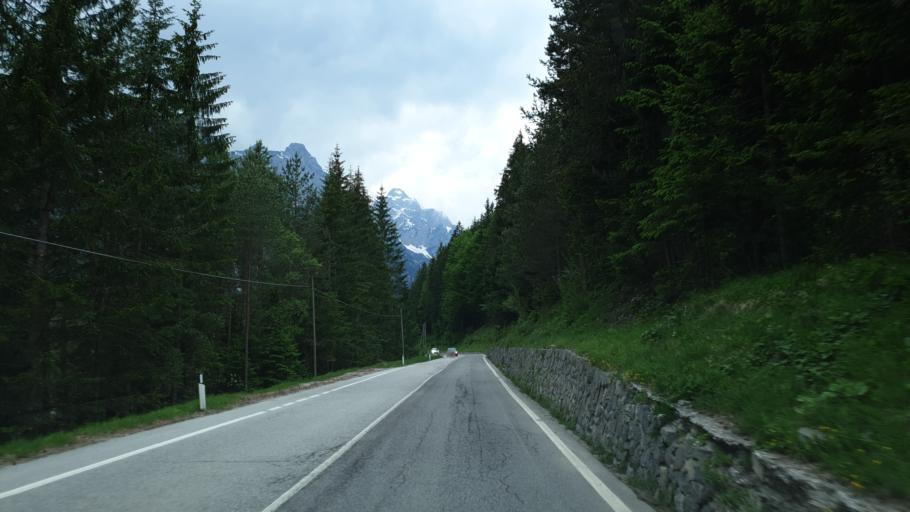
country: IT
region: Veneto
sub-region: Provincia di Belluno
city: Auronzo
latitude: 46.5509
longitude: 12.3312
